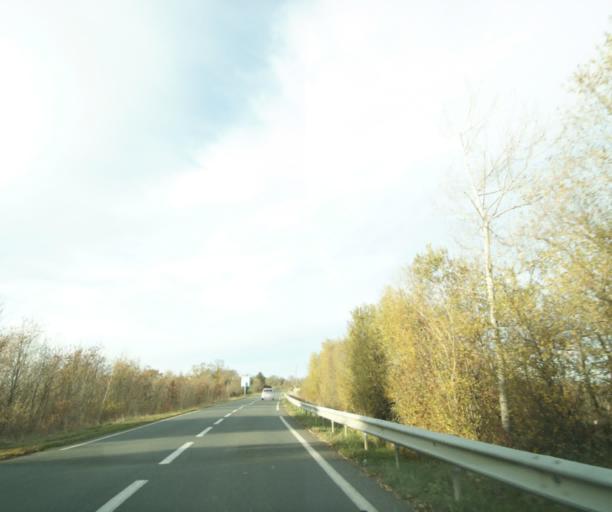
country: FR
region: Midi-Pyrenees
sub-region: Departement du Gers
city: Eauze
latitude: 43.7938
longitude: 0.1006
